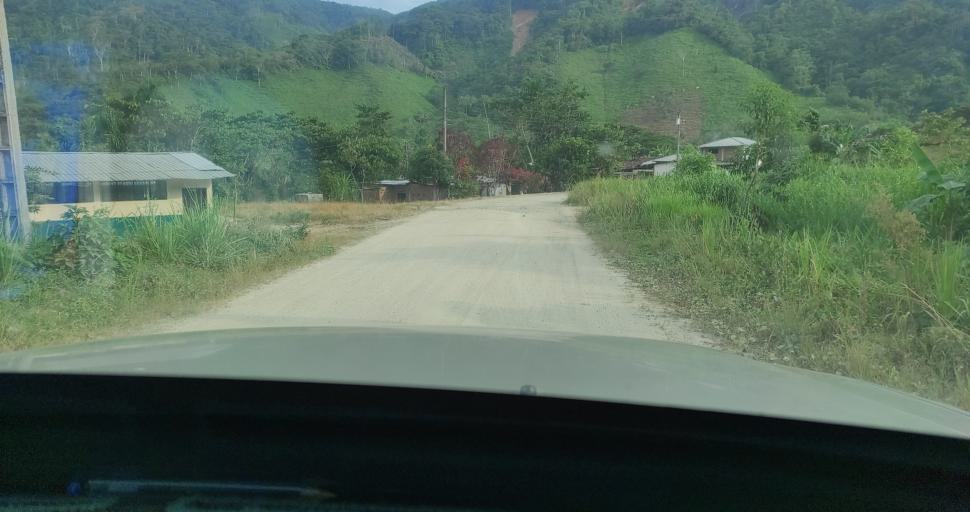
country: EC
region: Zamora-Chinchipe
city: Yantzaza
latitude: -3.7719
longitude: -78.8944
